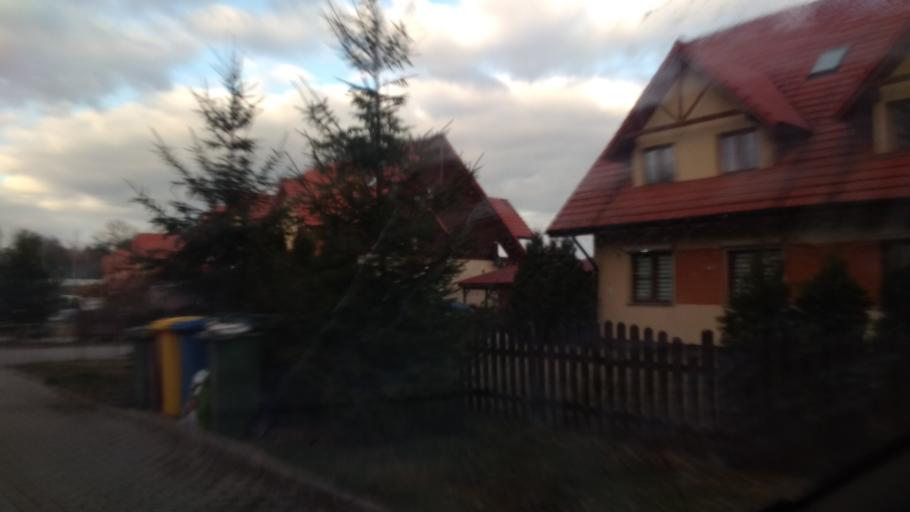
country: PL
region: Lower Silesian Voivodeship
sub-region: Jelenia Gora
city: Cieplice Slaskie Zdroj
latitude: 50.8550
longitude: 15.7139
